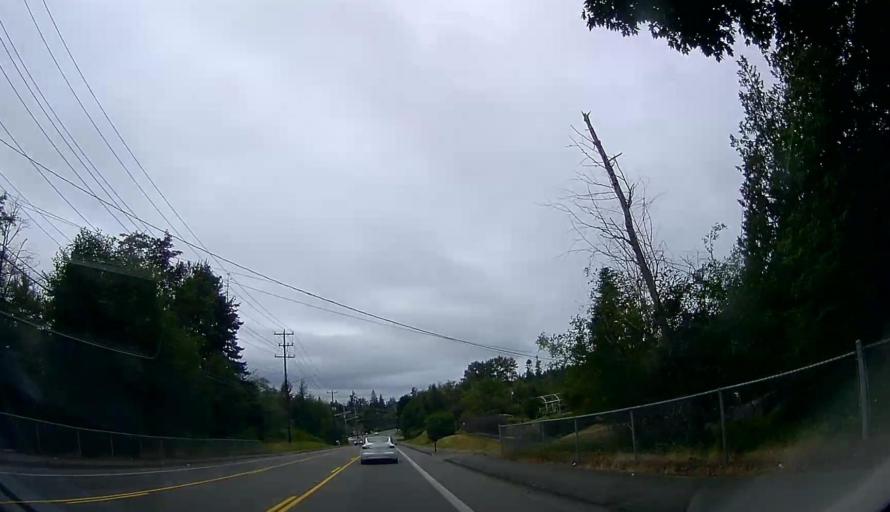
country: US
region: Washington
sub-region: Snohomish County
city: Tulalip
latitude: 48.0385
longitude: -122.2392
